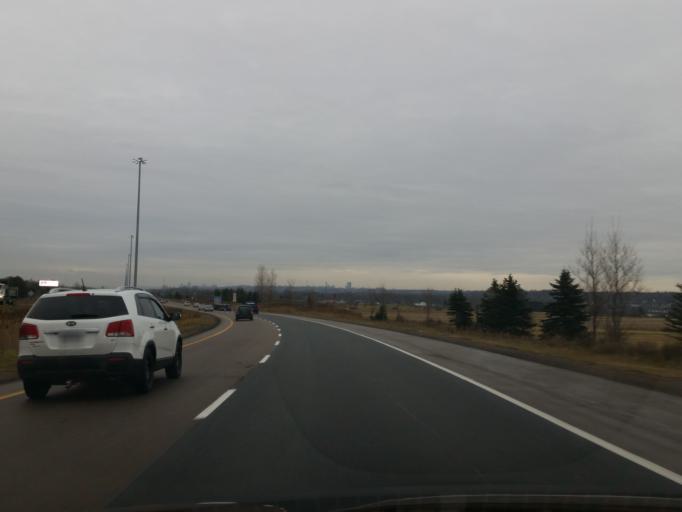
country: CA
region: Quebec
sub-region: Capitale-Nationale
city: Saint-Augustin-de-Desmaures
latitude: 46.7518
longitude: -71.4125
